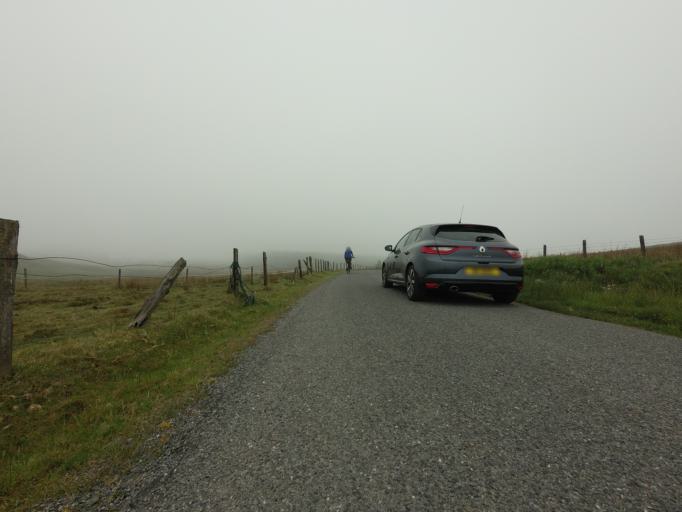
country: GB
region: Scotland
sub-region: Perth and Kinross
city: Kinross
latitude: 56.1528
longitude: -3.4535
